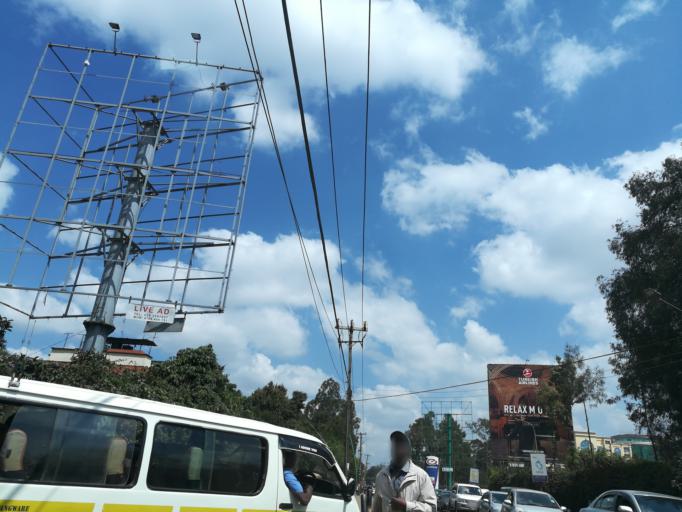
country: KE
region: Nairobi Area
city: Nairobi
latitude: -1.2923
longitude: 36.7858
